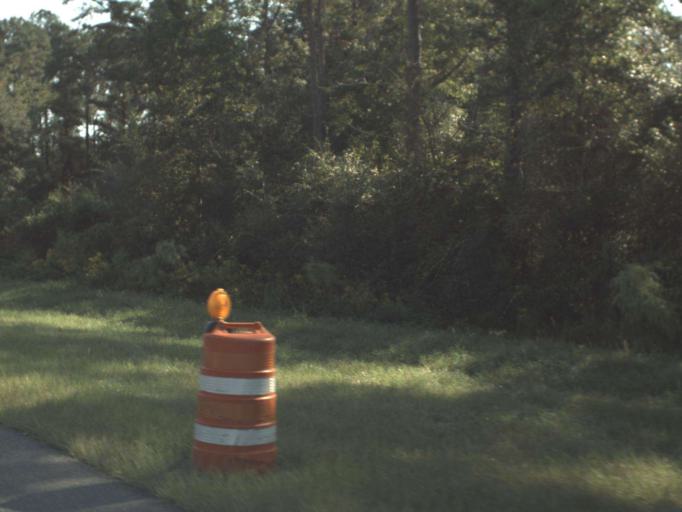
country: US
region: Florida
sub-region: Holmes County
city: Bonifay
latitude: 30.6343
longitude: -85.7081
